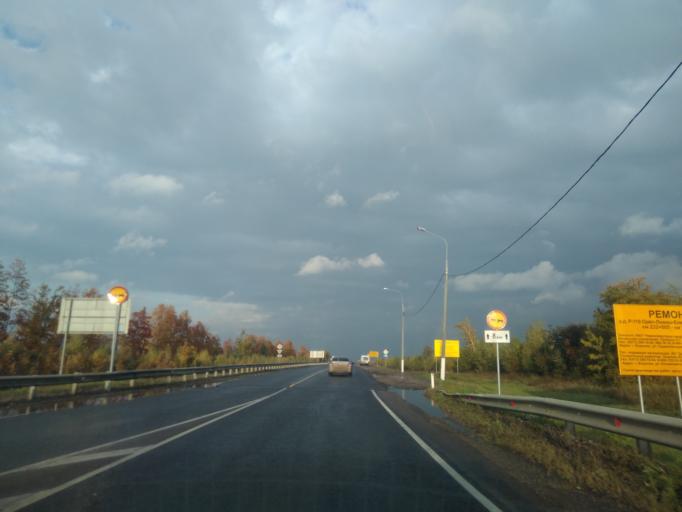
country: RU
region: Lipetsk
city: Yelets
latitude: 52.5469
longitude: 38.7219
